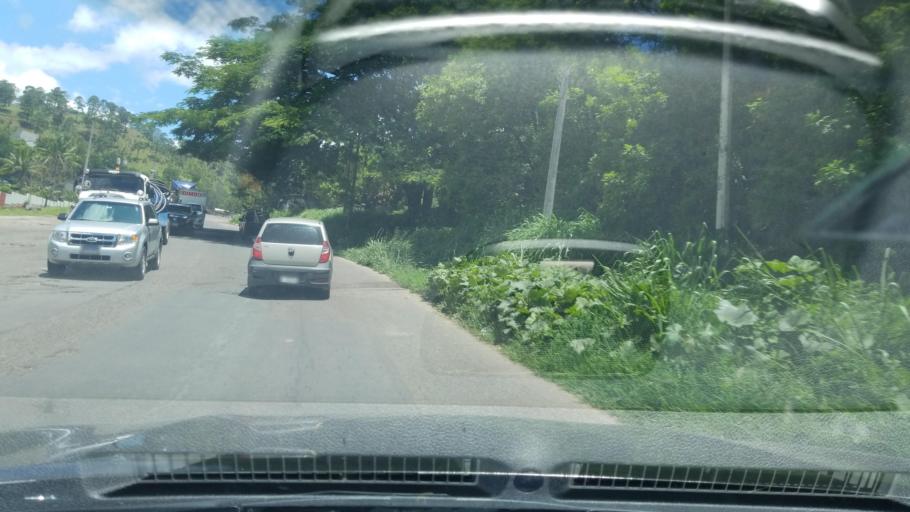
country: HN
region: Francisco Morazan
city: Rio Abajo
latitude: 14.1454
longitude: -87.2239
